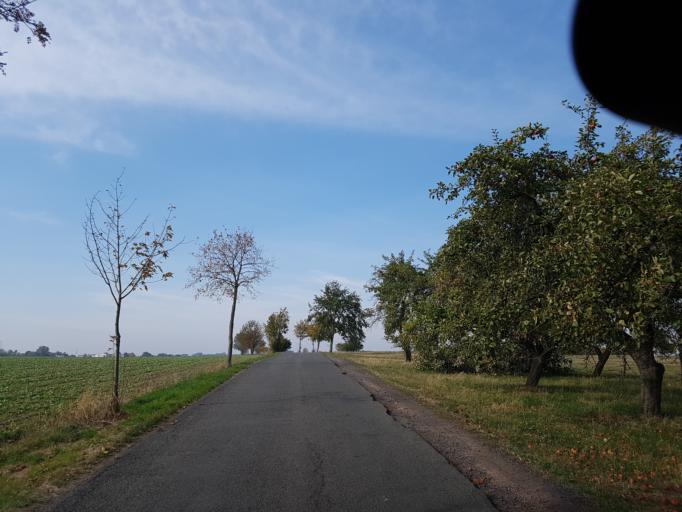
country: DE
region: Saxony
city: Hartha
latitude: 51.0920
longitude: 12.9973
